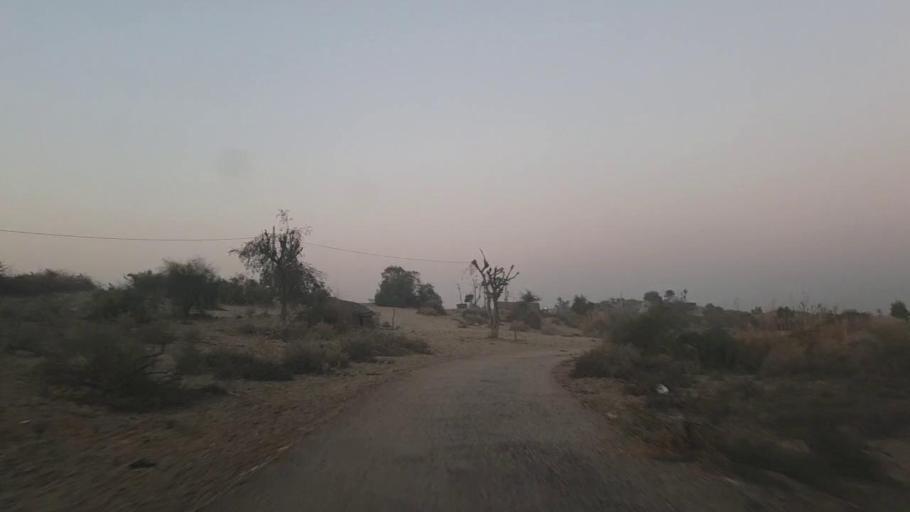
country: PK
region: Sindh
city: Jam Sahib
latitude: 26.3899
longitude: 68.8199
